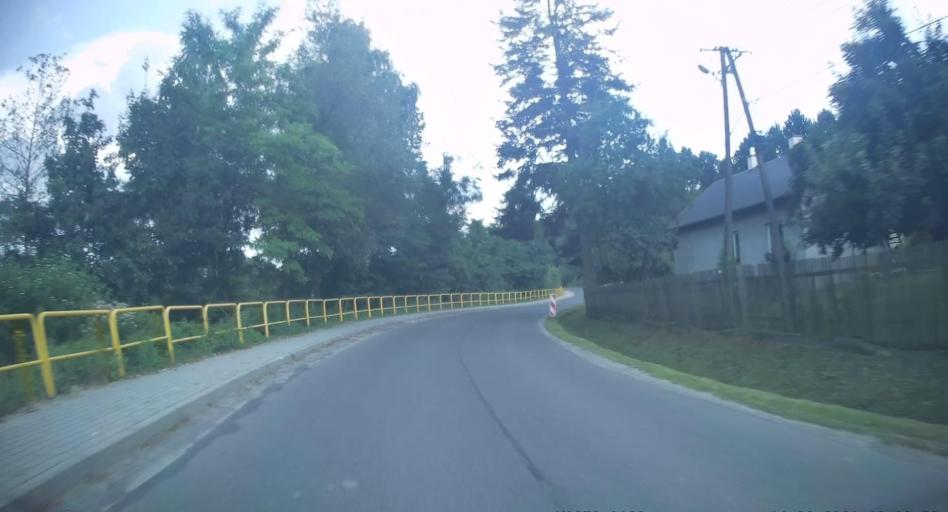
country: PL
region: Subcarpathian Voivodeship
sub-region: Powiat debicki
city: Debica
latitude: 49.9948
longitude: 21.4206
